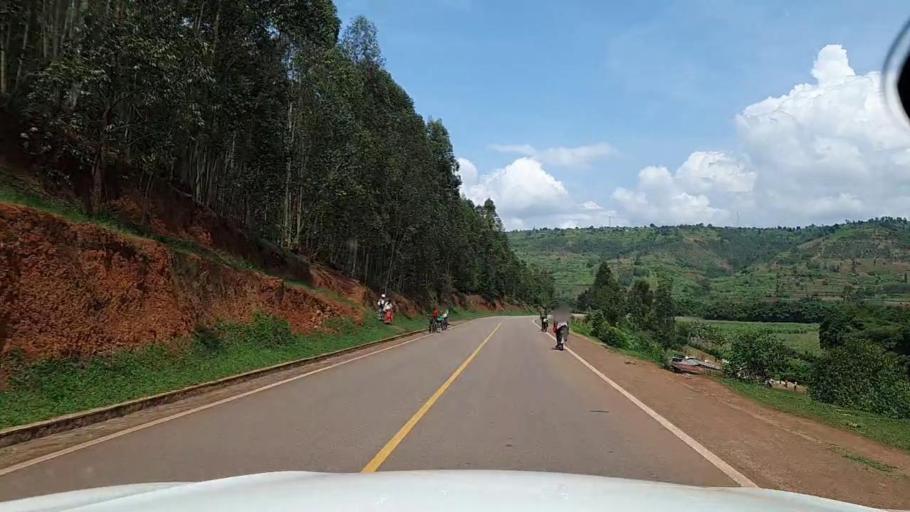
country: RW
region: Kigali
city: Kigali
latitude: -1.8492
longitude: 30.0966
